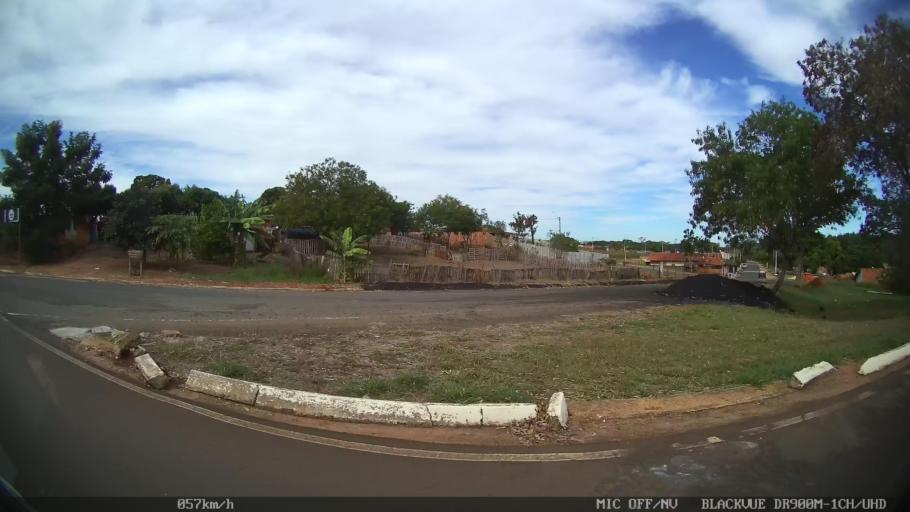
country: BR
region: Sao Paulo
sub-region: Santa Adelia
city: Santa Adelia
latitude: -21.3687
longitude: -48.7470
